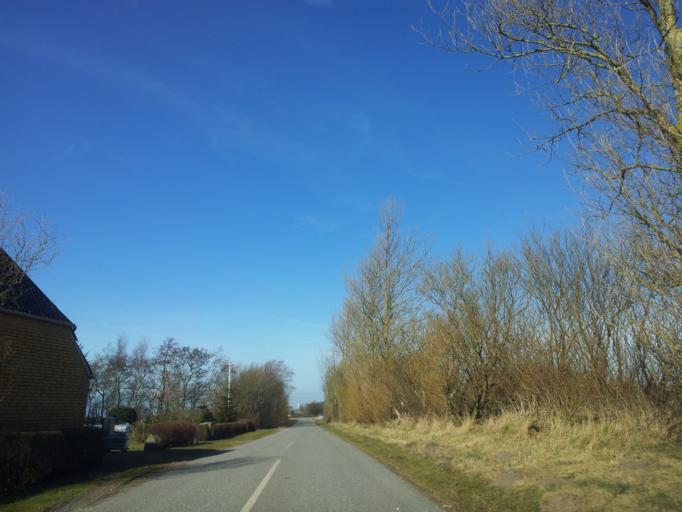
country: DK
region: South Denmark
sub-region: Tonder Kommune
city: Sherrebek
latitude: 55.1825
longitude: 8.7169
